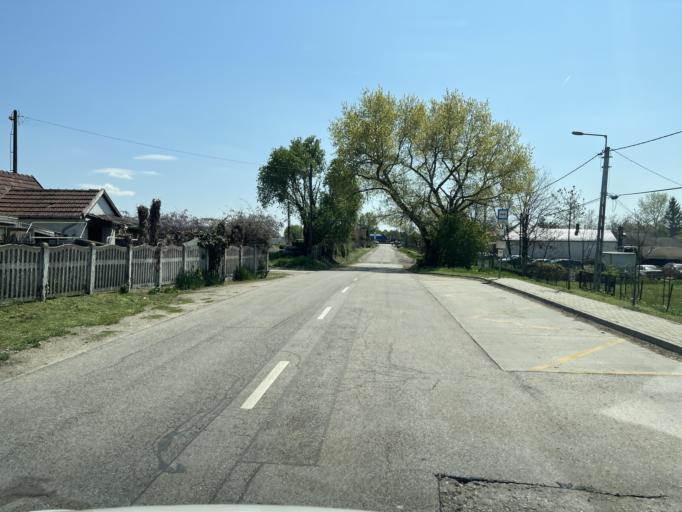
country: HU
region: Pest
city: Dabas
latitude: 47.1945
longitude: 19.3291
